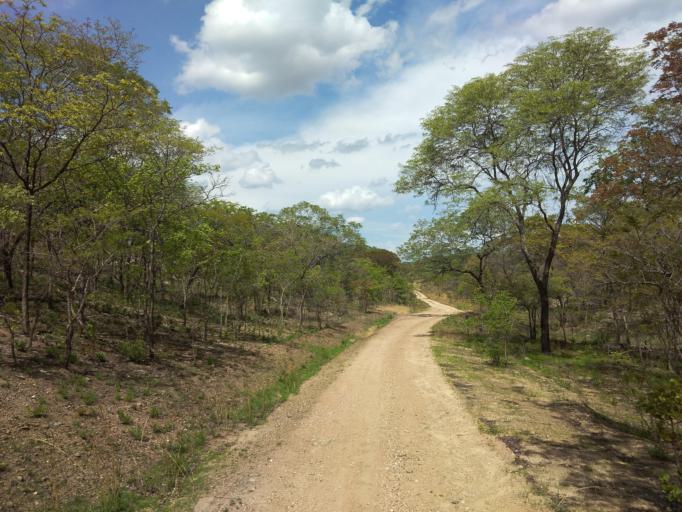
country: ZM
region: Eastern
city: Nyimba
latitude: -14.1223
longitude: 30.0963
